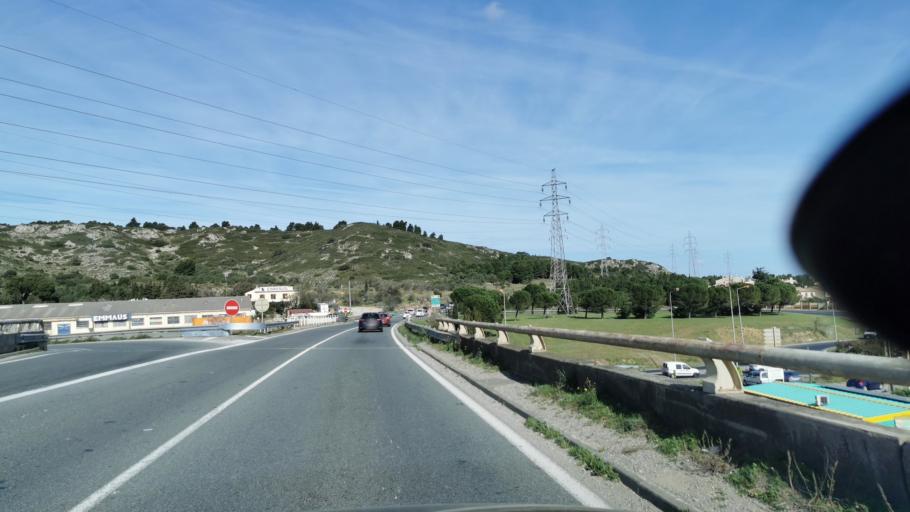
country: FR
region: Languedoc-Roussillon
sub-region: Departement de l'Aude
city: Narbonne
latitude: 43.1802
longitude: 2.9675
